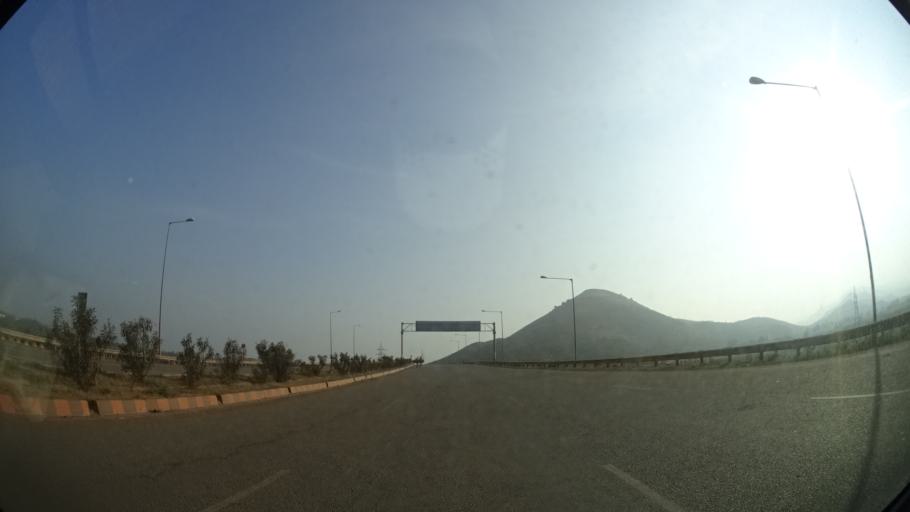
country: IN
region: Karnataka
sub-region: Bellary
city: Hospet
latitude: 15.2497
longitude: 76.3702
